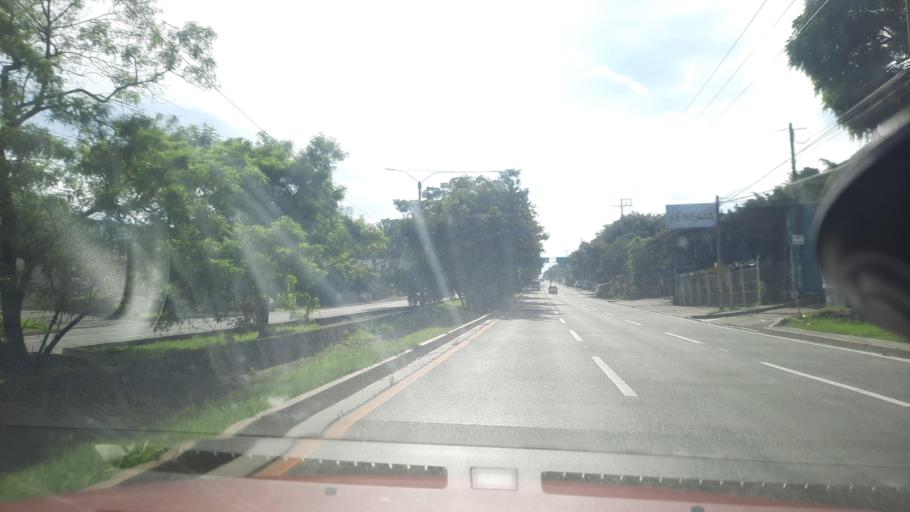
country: SV
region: San Salvador
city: San Marcos
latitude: 13.6495
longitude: -89.1799
